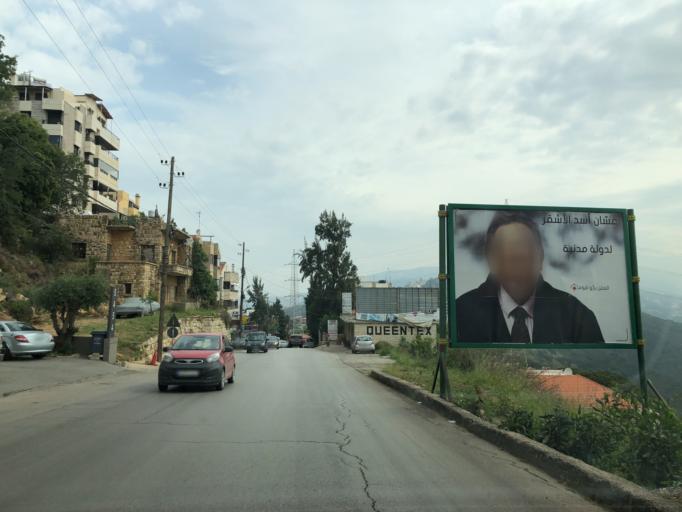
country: LB
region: Mont-Liban
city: Jdaidet el Matn
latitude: 33.8708
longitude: 35.6100
